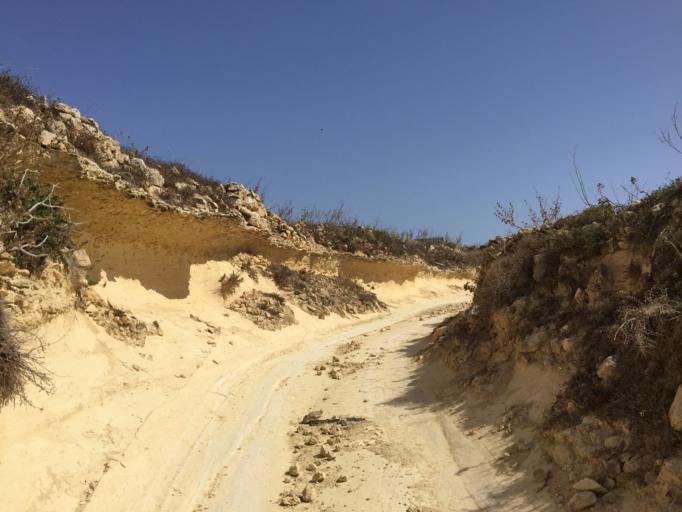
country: MT
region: L-Gharb
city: Gharb
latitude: 36.0725
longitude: 14.2008
